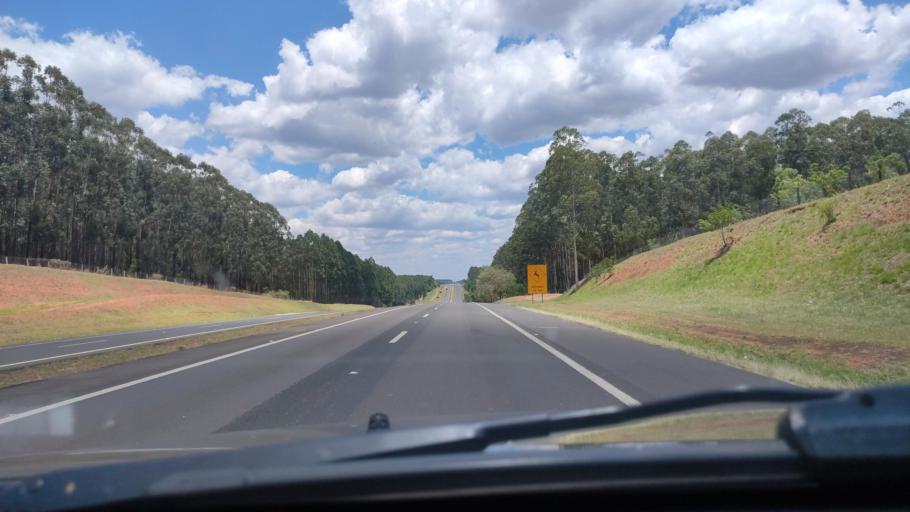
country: BR
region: Sao Paulo
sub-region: Duartina
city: Duartina
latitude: -22.4903
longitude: -49.2495
